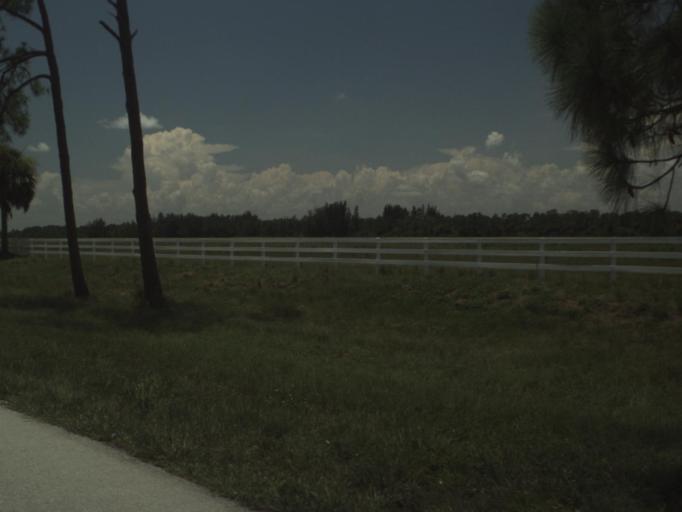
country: US
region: Florida
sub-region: Martin County
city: Indiantown
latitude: 27.0447
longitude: -80.3550
